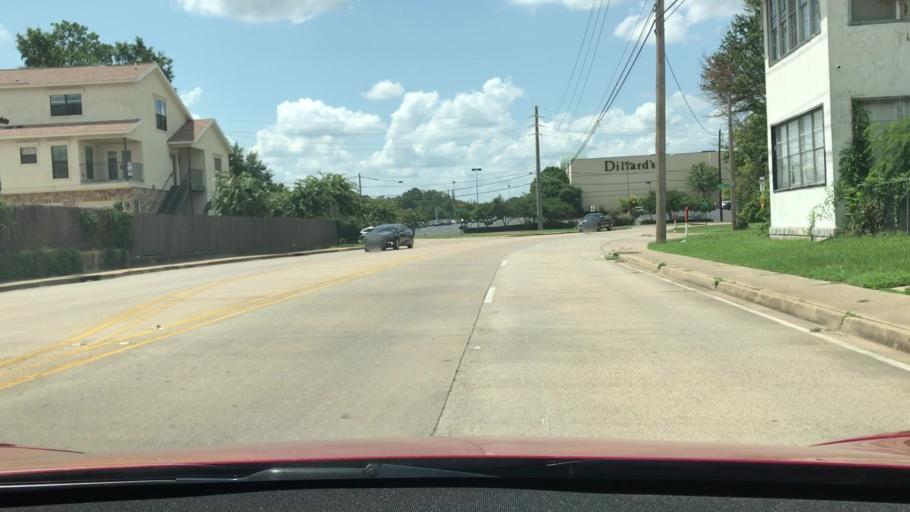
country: US
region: Louisiana
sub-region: Bossier Parish
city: Bossier City
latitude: 32.4811
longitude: -93.7522
